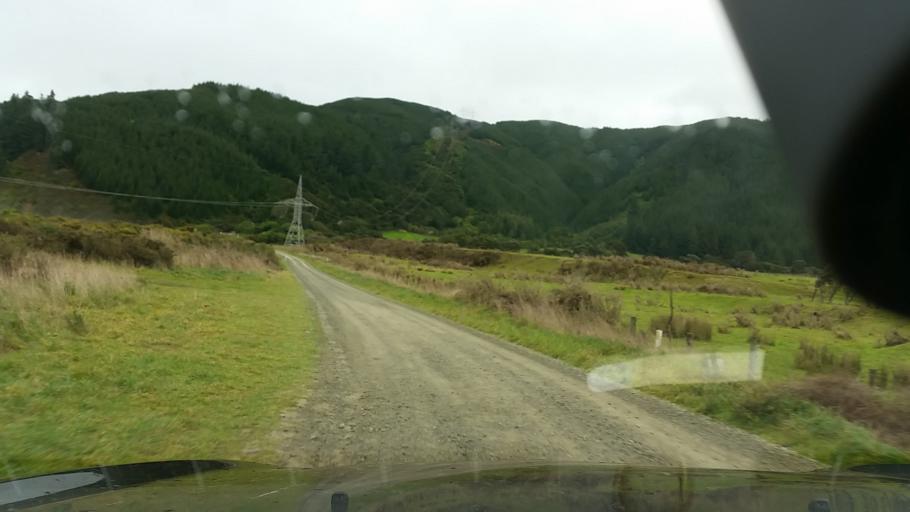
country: NZ
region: Marlborough
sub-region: Marlborough District
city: Picton
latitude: -41.3552
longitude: 174.0708
